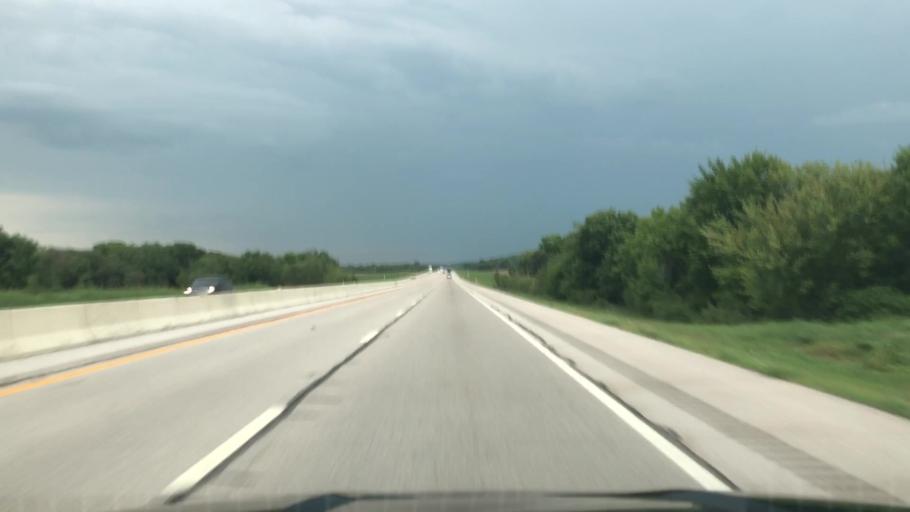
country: US
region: Oklahoma
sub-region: Rogers County
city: Bushyhead
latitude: 36.3748
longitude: -95.4401
